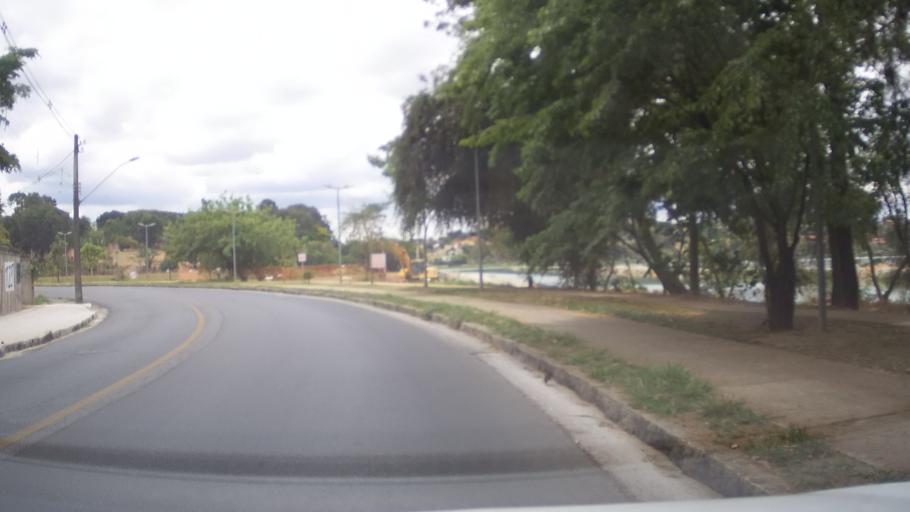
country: BR
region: Minas Gerais
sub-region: Belo Horizonte
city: Belo Horizonte
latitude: -19.8490
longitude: -43.9959
